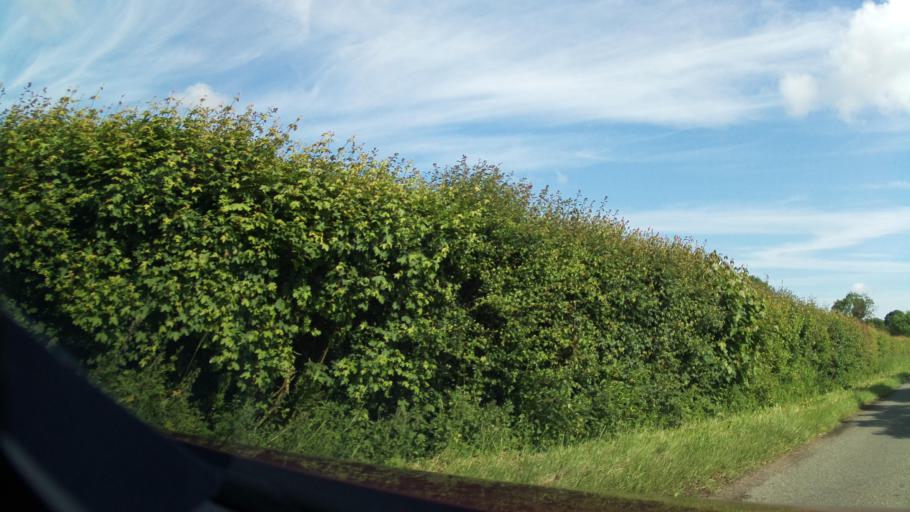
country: GB
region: England
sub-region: Lincolnshire
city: Skellingthorpe
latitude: 53.1356
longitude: -0.6332
